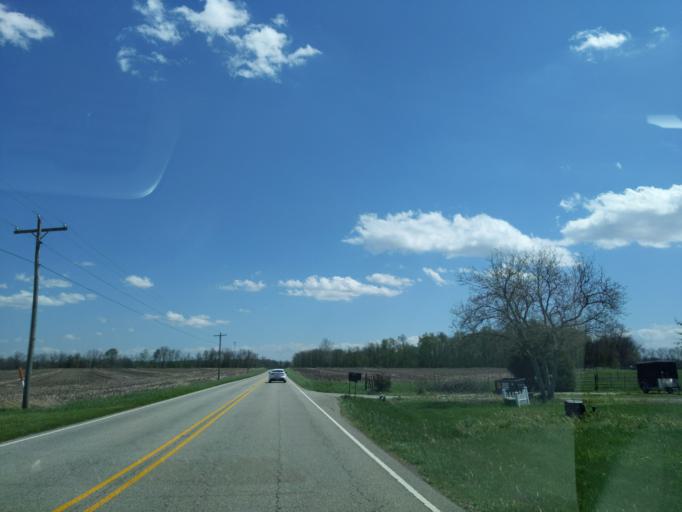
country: US
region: Indiana
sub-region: Decatur County
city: Saint Paul
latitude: 39.3991
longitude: -85.5579
